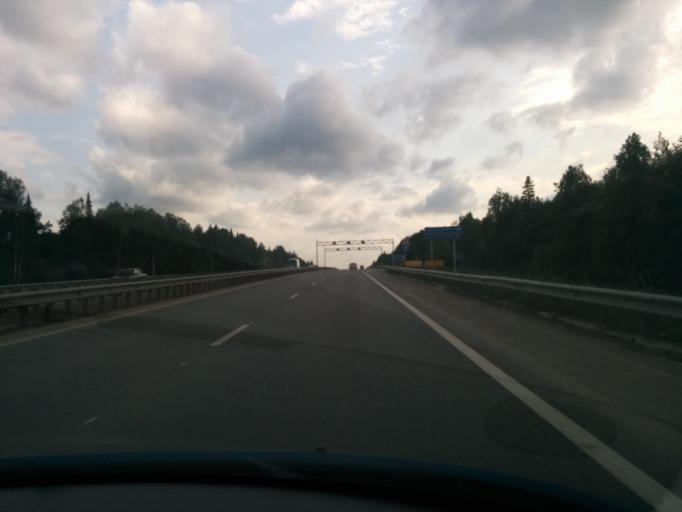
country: RU
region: Perm
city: Ferma
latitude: 58.0281
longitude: 56.4295
